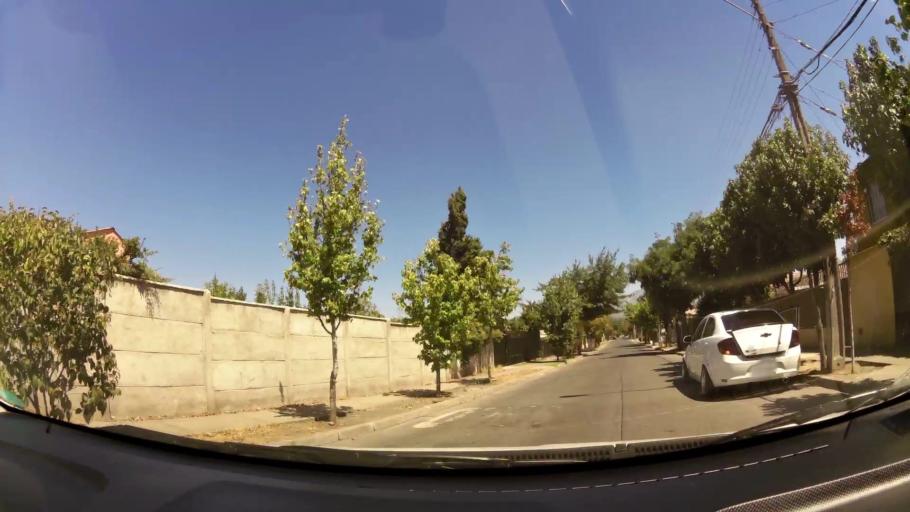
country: CL
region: O'Higgins
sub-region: Provincia de Cachapoal
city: Rancagua
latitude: -34.1607
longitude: -70.7508
